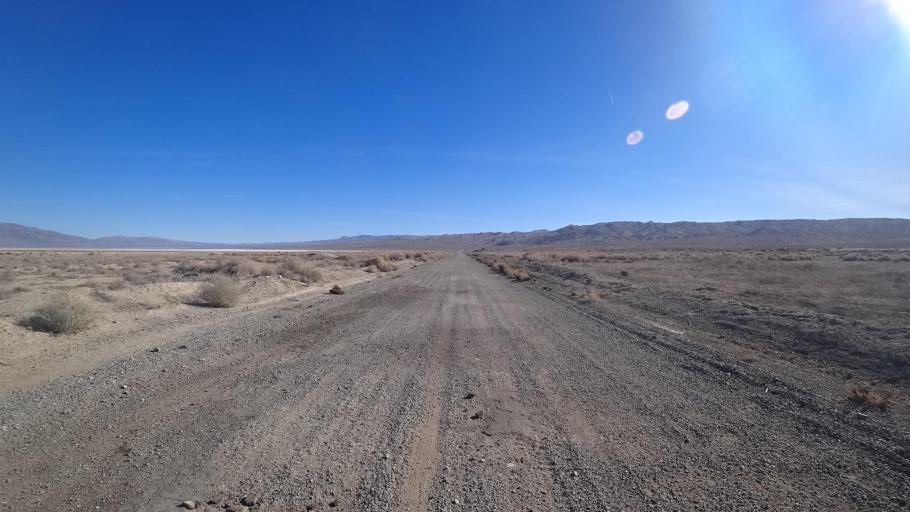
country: US
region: California
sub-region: Kern County
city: California City
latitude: 35.2871
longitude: -117.9104
